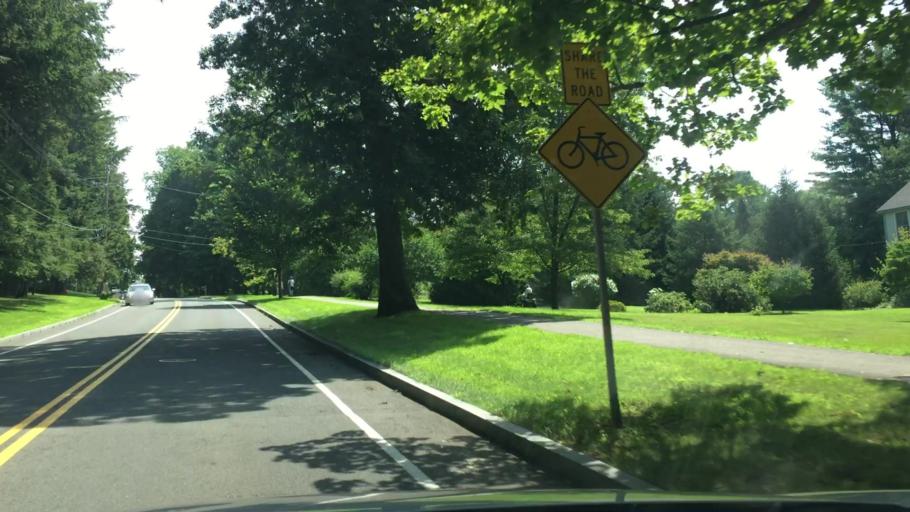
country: US
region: Massachusetts
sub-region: Berkshire County
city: Lenox
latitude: 42.3569
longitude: -73.2891
